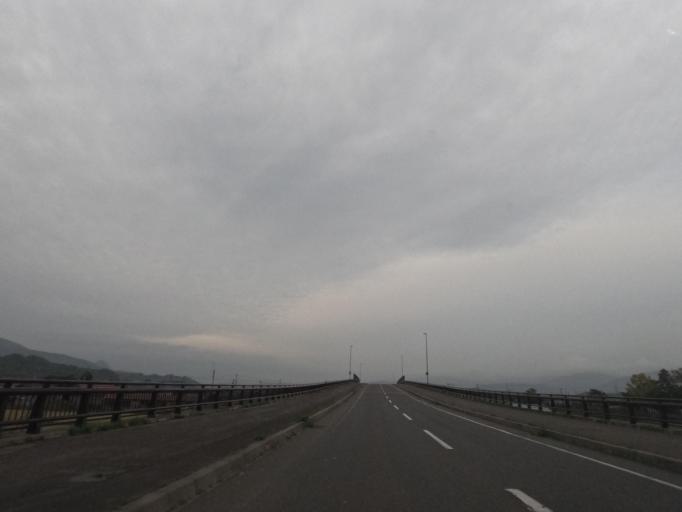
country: JP
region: Hokkaido
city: Date
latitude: 42.4884
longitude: 140.8298
